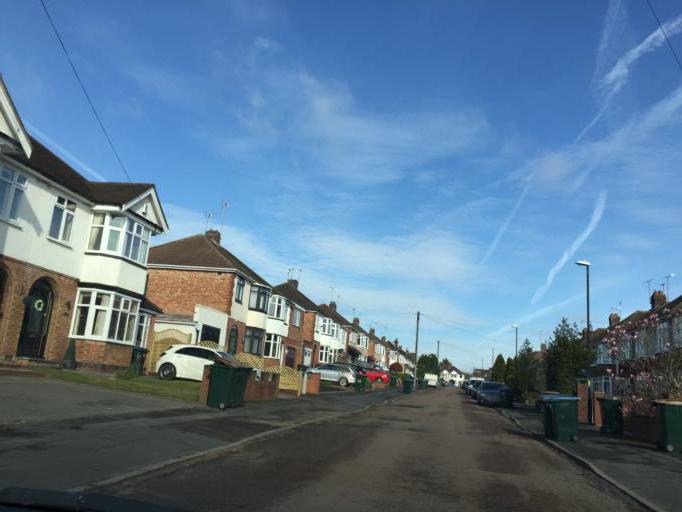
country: GB
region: England
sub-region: Coventry
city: Coventry
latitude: 52.3827
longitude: -1.5099
